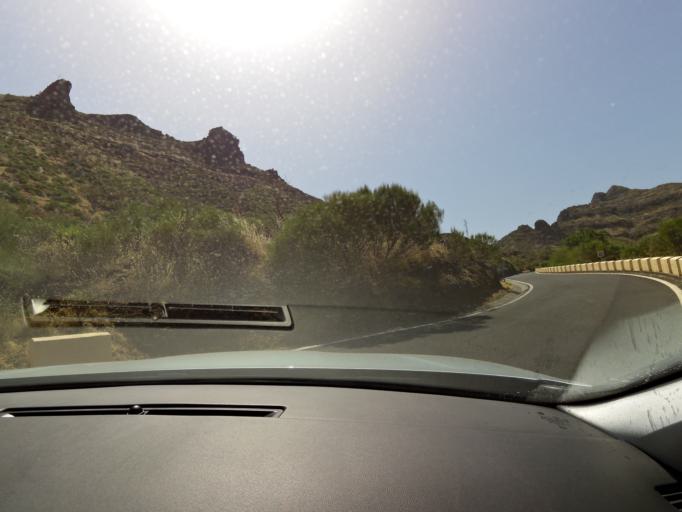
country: ES
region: Canary Islands
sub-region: Provincia de Santa Cruz de Tenerife
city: Santiago del Teide
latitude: 28.2969
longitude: -16.8184
